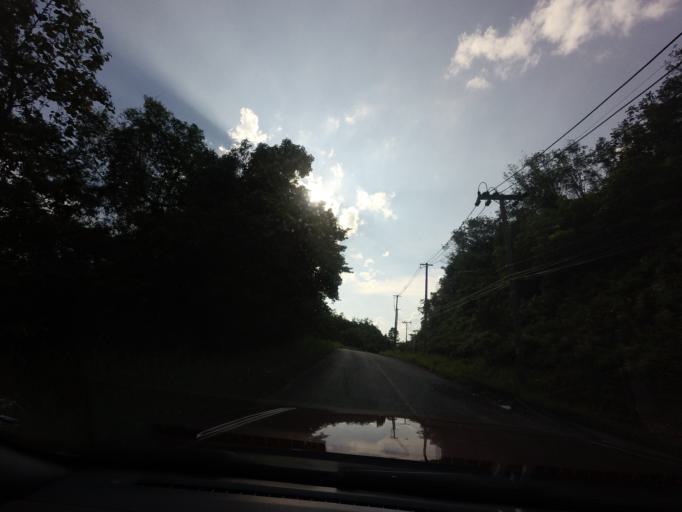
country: TH
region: Yala
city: Than To
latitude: 6.1447
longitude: 101.2853
